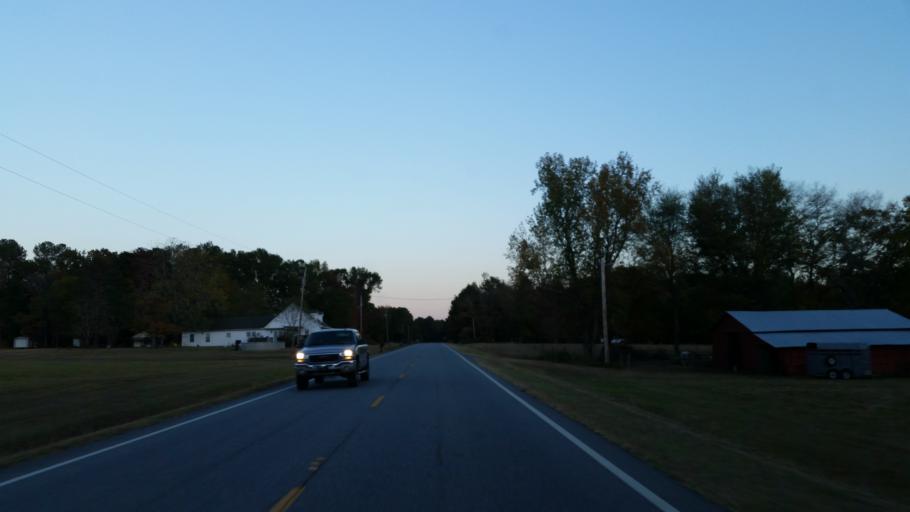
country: US
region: Georgia
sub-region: Gordon County
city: Calhoun
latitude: 34.5960
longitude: -85.0302
